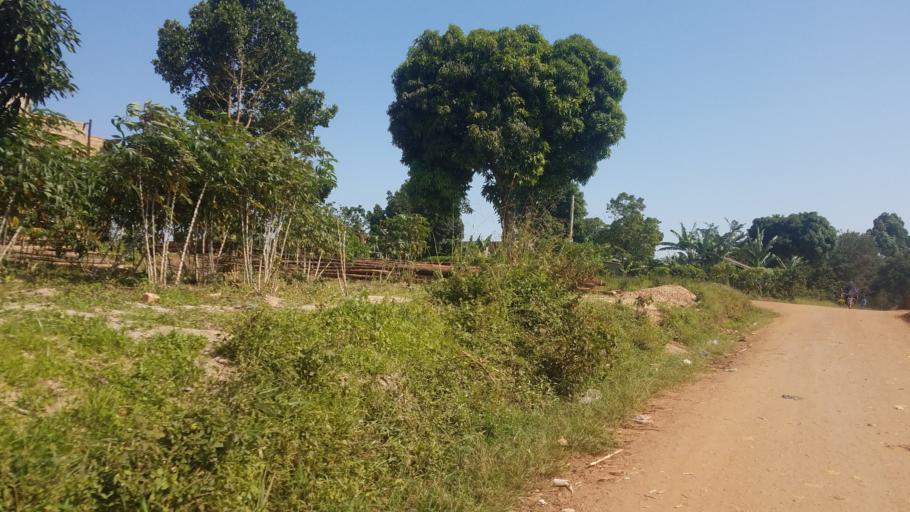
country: UG
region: Central Region
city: Masaka
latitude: -0.3283
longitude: 31.7093
